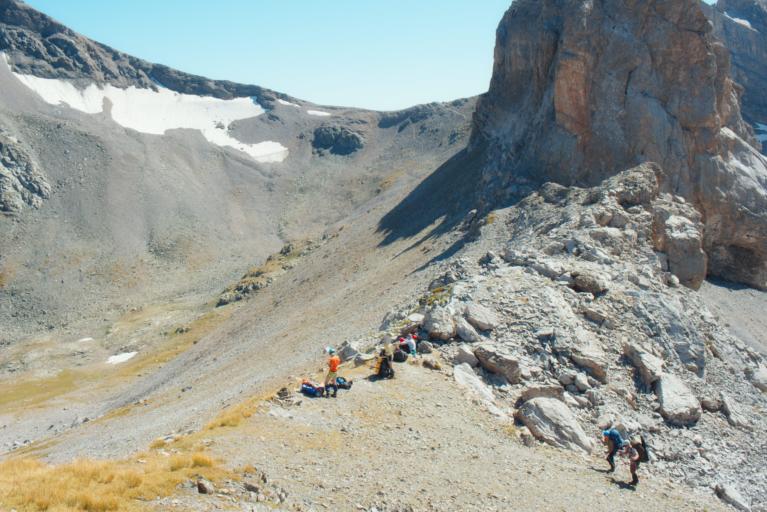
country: RU
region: Karachayevo-Cherkesiya
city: Nizhniy Arkhyz
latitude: 43.5943
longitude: 41.1861
